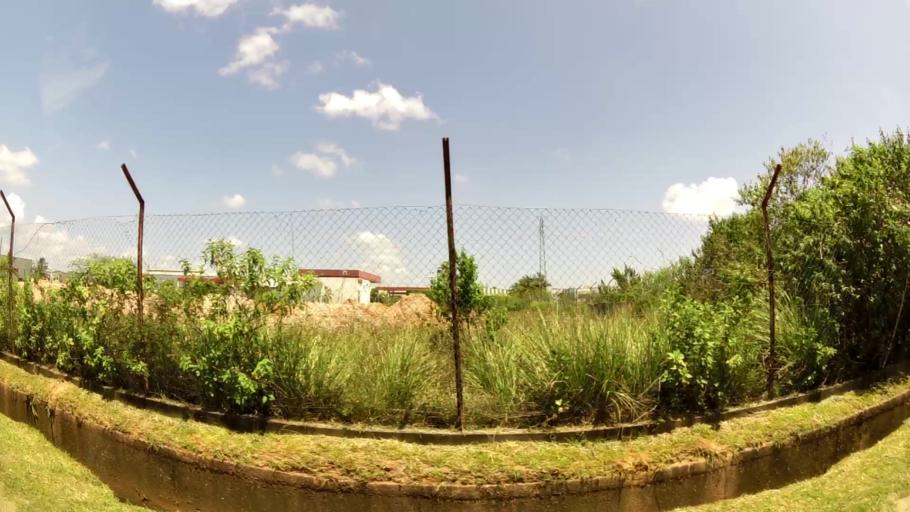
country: GF
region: Guyane
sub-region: Guyane
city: Cayenne
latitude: 4.9031
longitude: -52.3233
